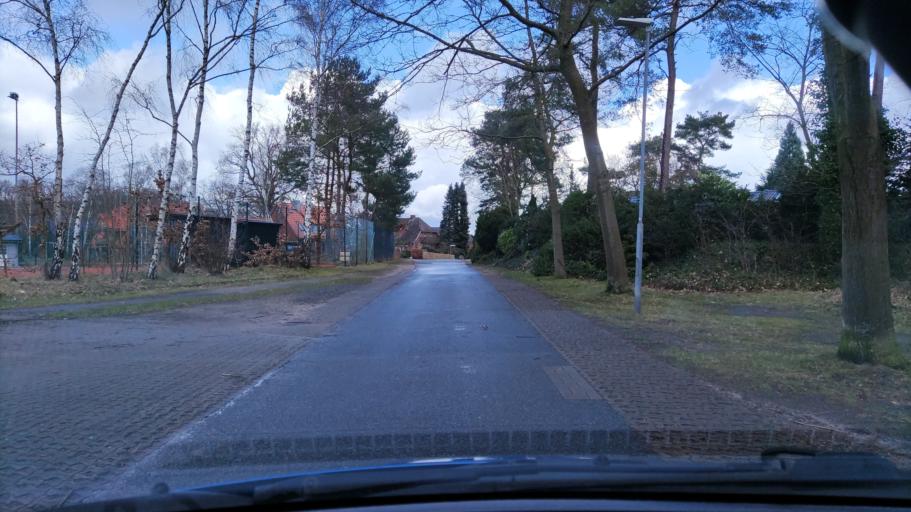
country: DE
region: Lower Saxony
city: Winsen
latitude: 53.3275
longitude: 10.2023
